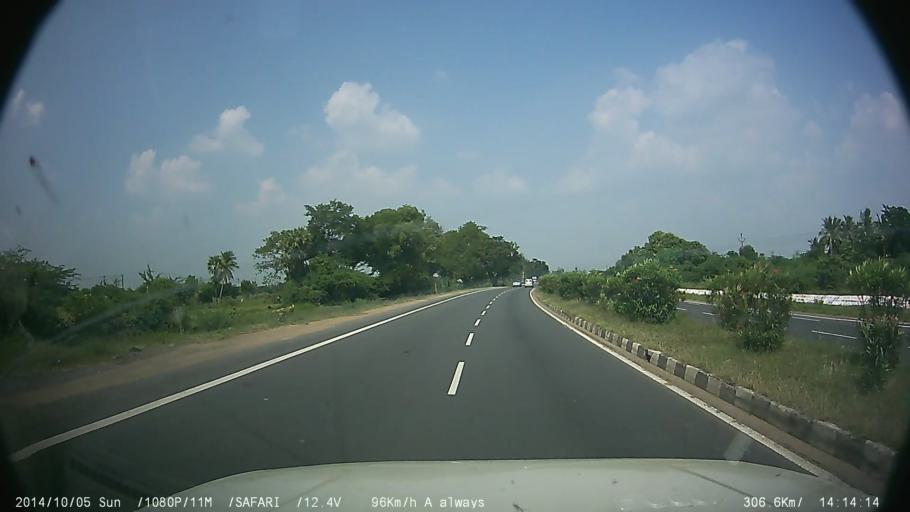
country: IN
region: Tamil Nadu
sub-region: Villupuram
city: Tindivanam
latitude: 12.2679
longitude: 79.6851
